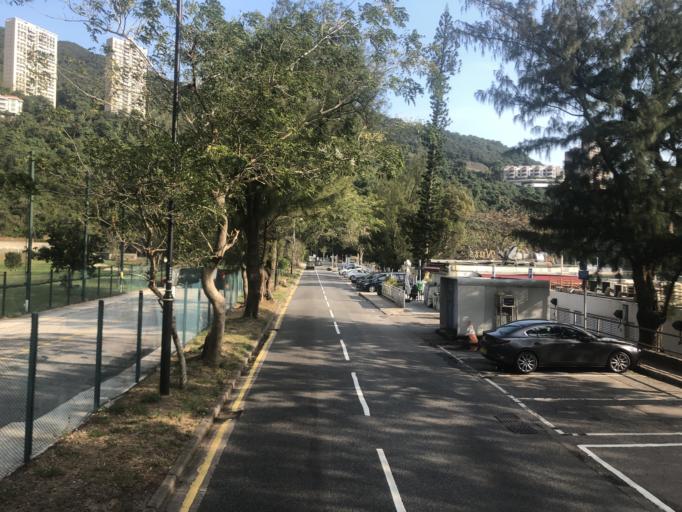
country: HK
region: Wanchai
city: Wan Chai
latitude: 22.2455
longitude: 114.1869
